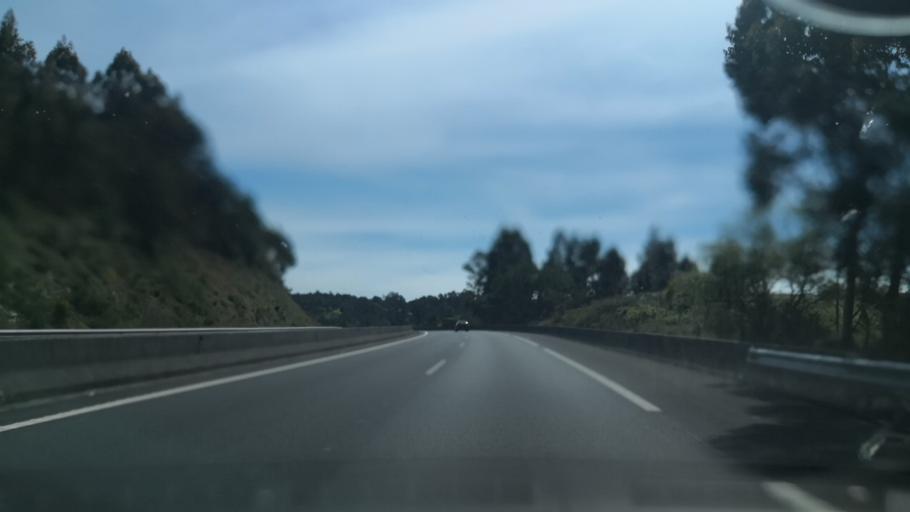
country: ES
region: Galicia
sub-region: Provincia de Pontevedra
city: Valga
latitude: 42.6834
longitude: -8.6339
